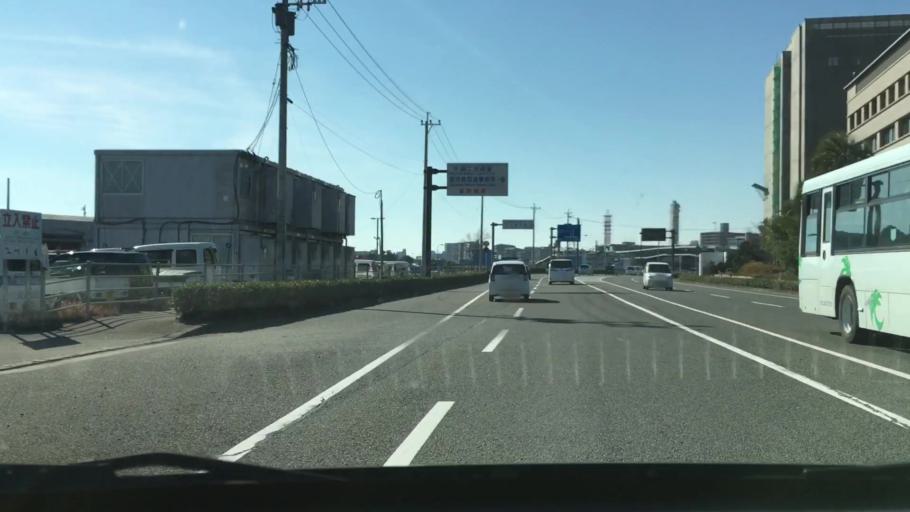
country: JP
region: Kagoshima
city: Kagoshima-shi
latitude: 31.6004
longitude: 130.5651
